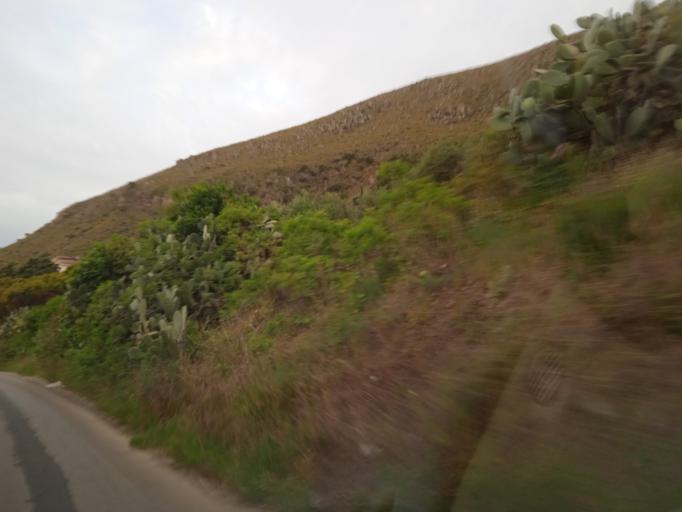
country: IT
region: Sicily
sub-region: Palermo
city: Portella di Mare
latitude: 38.0574
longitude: 13.4613
